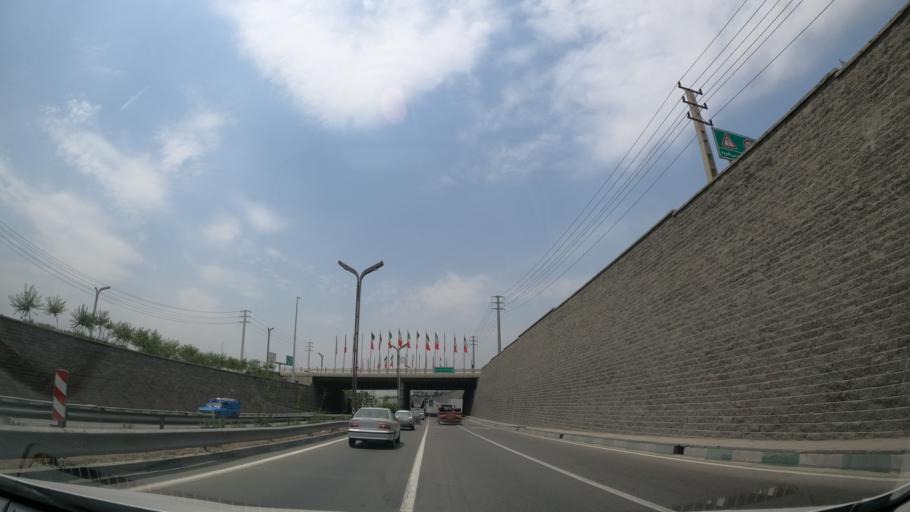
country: IR
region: Tehran
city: Shahr-e Qods
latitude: 35.7030
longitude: 51.1846
